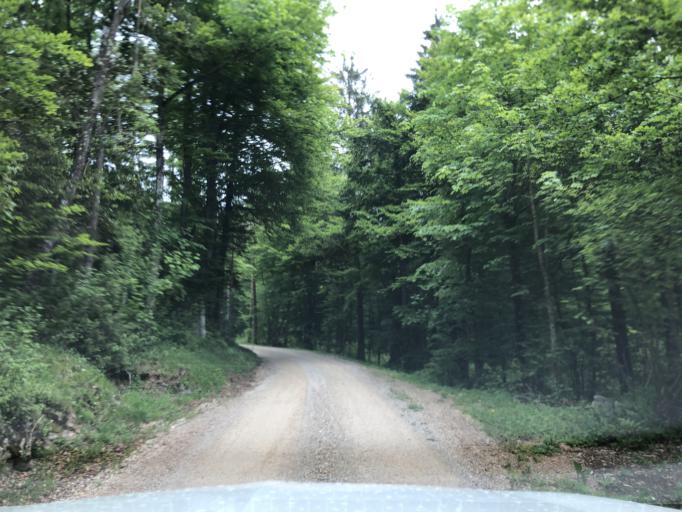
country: SI
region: Bloke
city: Nova Vas
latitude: 45.7526
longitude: 14.4640
